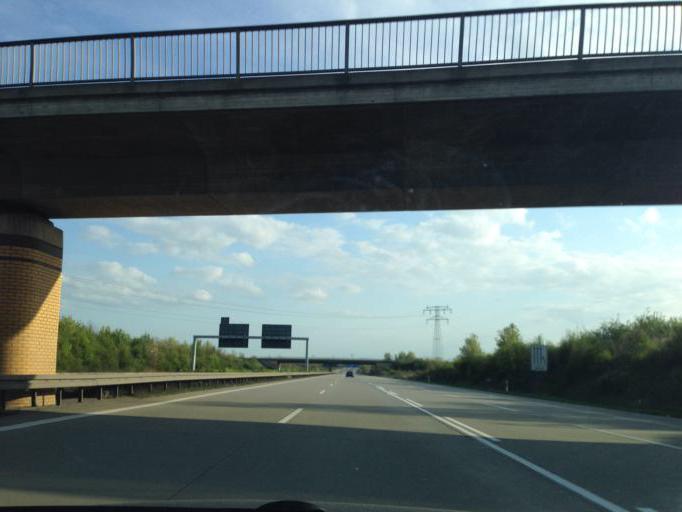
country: DE
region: Saxony-Anhalt
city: Diesdorf
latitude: 52.1599
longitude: 11.5445
